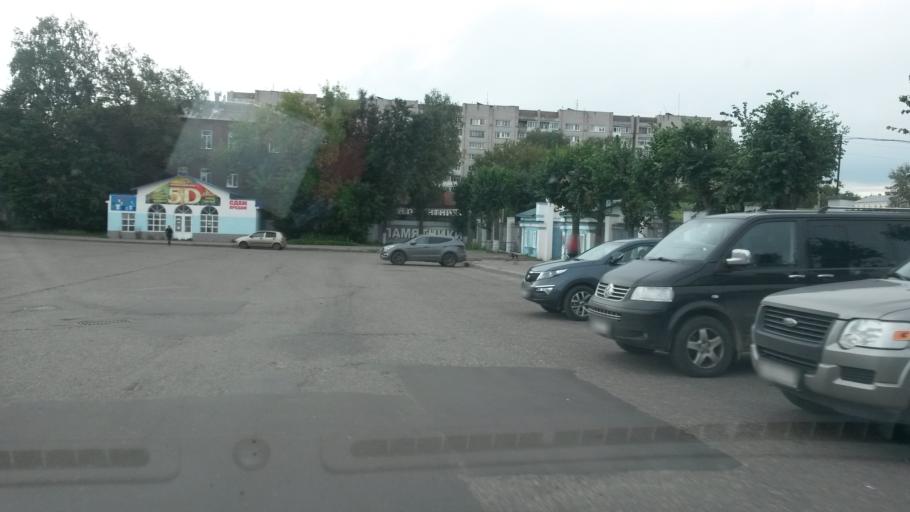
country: RU
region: Ivanovo
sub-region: Gorod Ivanovo
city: Ivanovo
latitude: 57.0204
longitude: 40.9509
